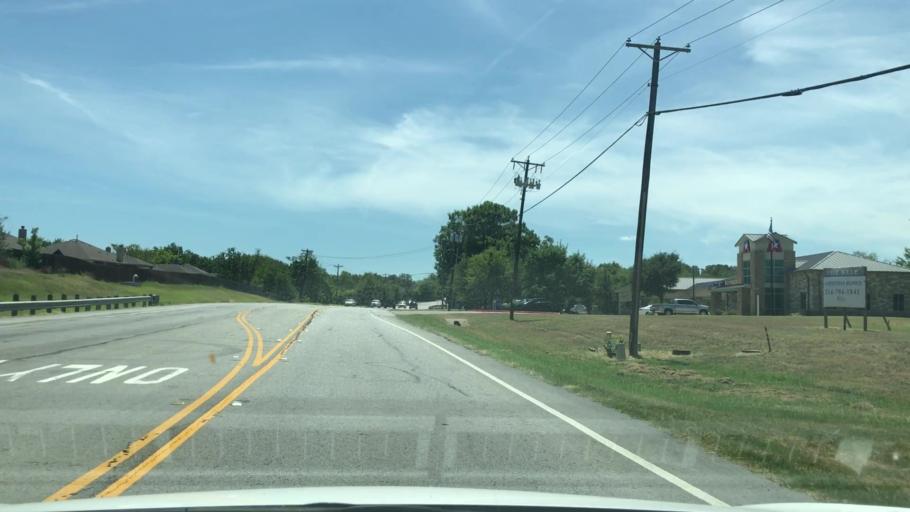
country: US
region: Texas
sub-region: Rockwall County
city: Rockwall
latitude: 32.9429
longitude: -96.4605
